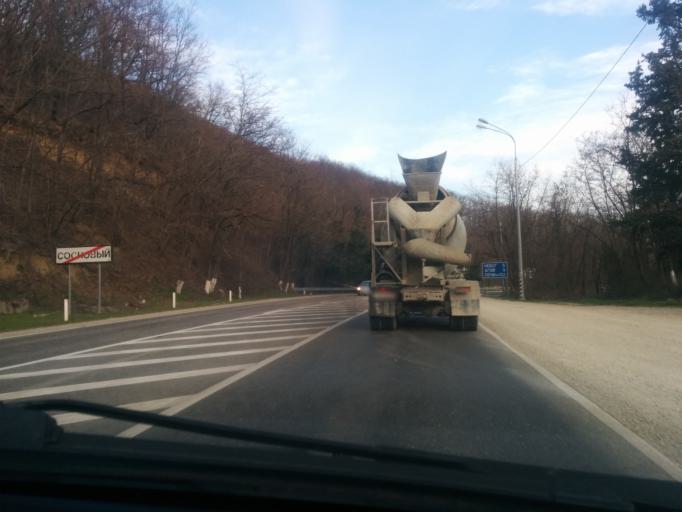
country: RU
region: Krasnodarskiy
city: Nebug
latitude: 44.1772
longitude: 38.9515
